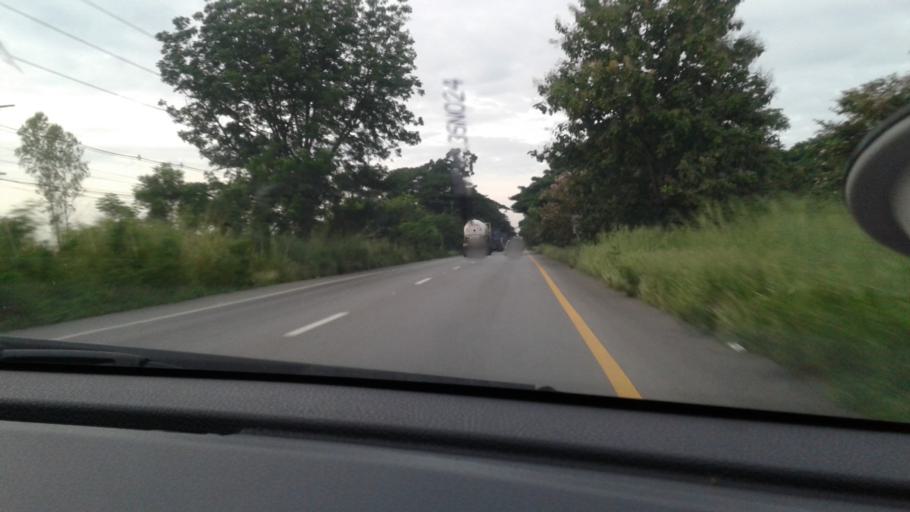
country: TH
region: Prachuap Khiri Khan
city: Hua Hin
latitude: 12.5210
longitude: 99.8812
